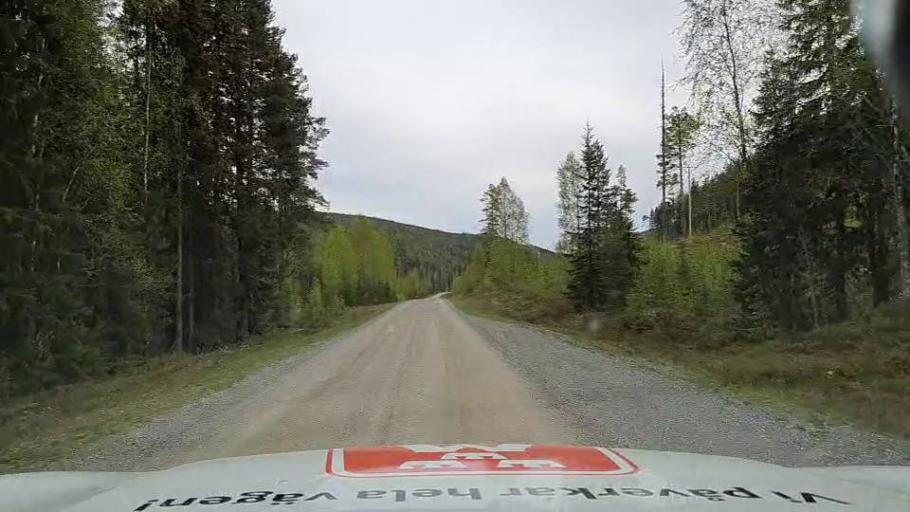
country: SE
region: Jaemtland
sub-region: Bergs Kommun
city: Hoverberg
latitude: 62.5315
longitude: 14.7076
